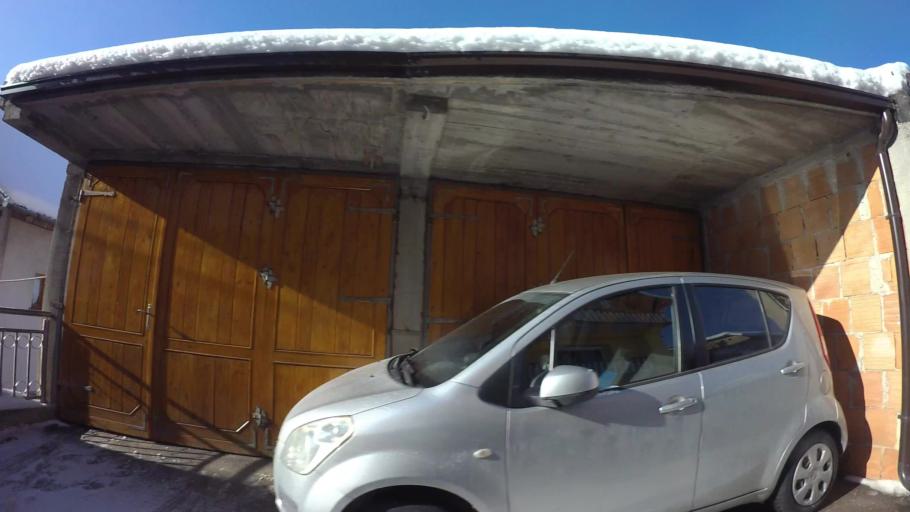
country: BA
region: Federation of Bosnia and Herzegovina
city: Kobilja Glava
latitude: 43.8750
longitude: 18.4224
